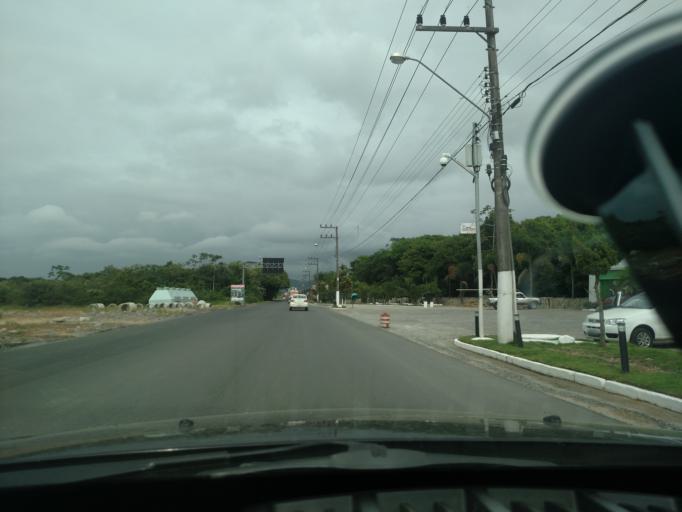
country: BR
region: Santa Catarina
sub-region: Porto Belo
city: Porto Belo
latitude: -27.1598
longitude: -48.6008
